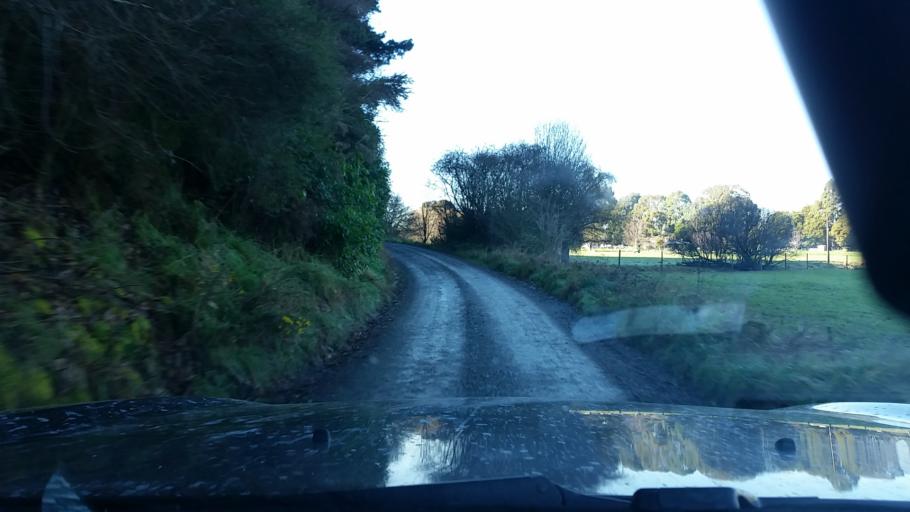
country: NZ
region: Marlborough
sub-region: Marlborough District
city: Blenheim
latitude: -41.4632
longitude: 173.7930
